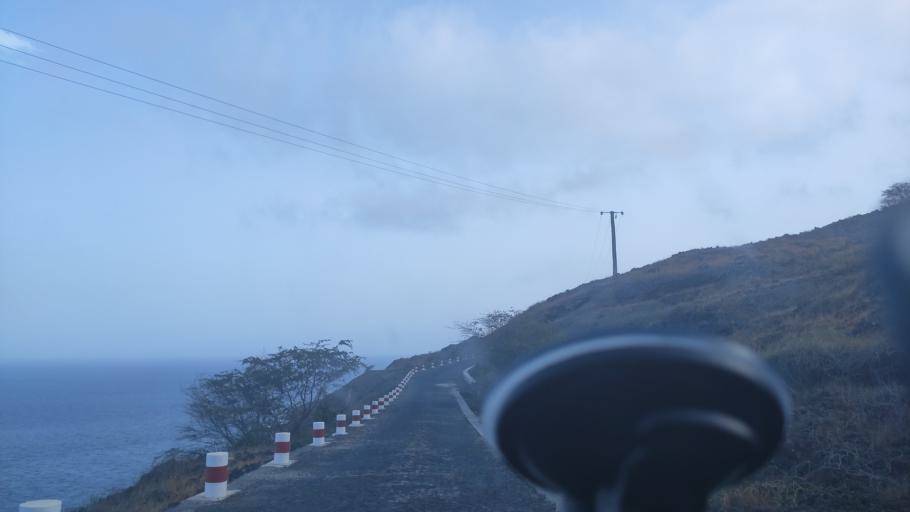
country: CV
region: Mosteiros
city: Porto dos Mosteiros
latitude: 15.0044
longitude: -24.3032
